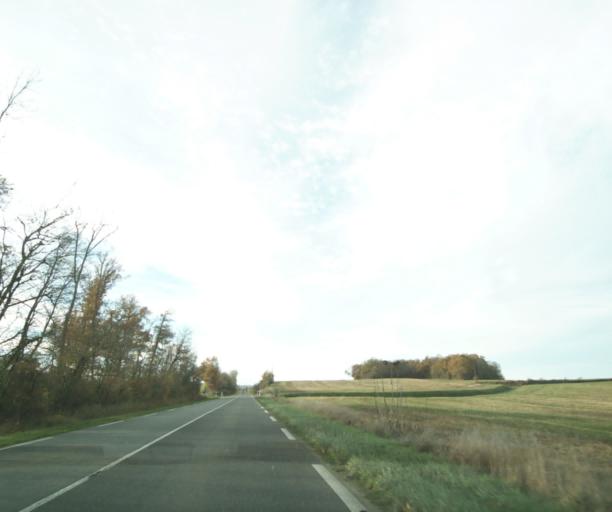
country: FR
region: Midi-Pyrenees
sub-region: Departement du Gers
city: Vic-Fezensac
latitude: 43.7547
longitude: 0.2492
